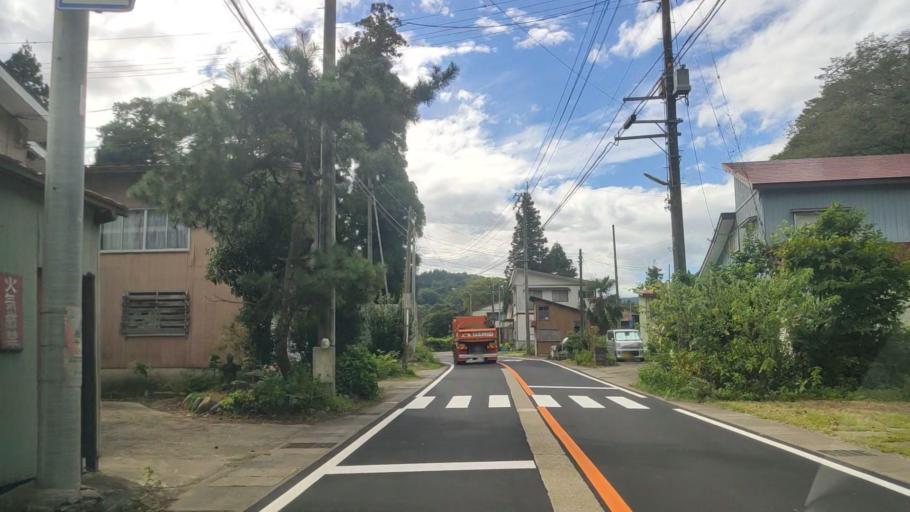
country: JP
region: Niigata
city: Arai
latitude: 36.9583
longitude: 138.2705
